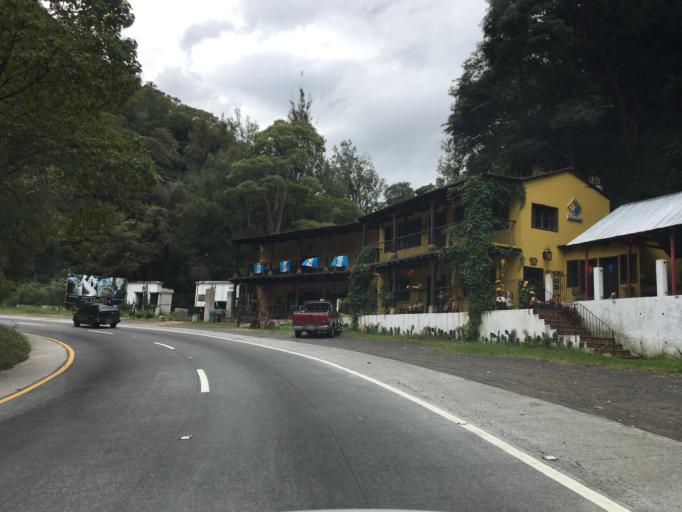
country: GT
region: Sacatepequez
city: Santa Lucia Milpas Altas
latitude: 14.5594
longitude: -90.6918
